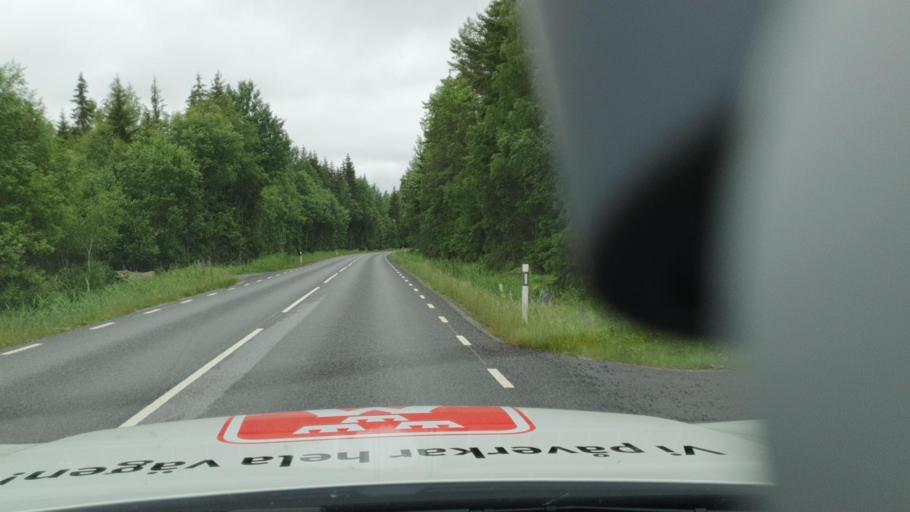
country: SE
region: OErebro
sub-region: Degerfors Kommun
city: Degerfors
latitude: 59.2283
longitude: 14.3966
